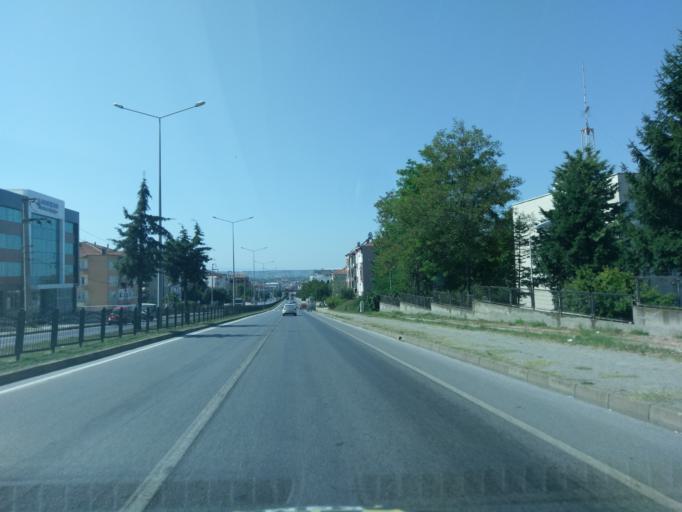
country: TR
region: Samsun
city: Bafra
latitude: 41.5559
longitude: 35.9145
